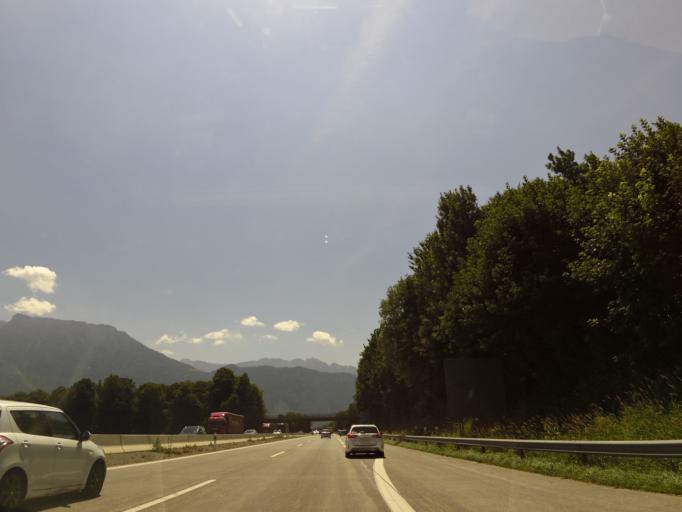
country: DE
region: Bavaria
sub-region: Upper Bavaria
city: Oberaudorf
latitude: 47.6486
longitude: 12.1885
